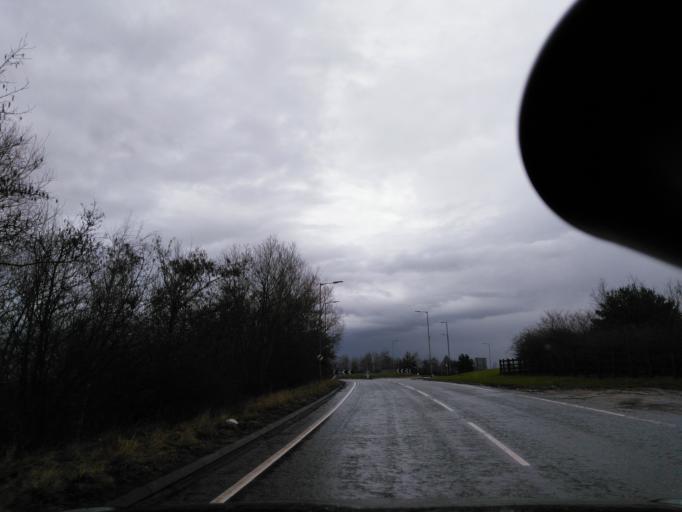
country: GB
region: England
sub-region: North Yorkshire
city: Boroughbridge
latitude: 54.1534
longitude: -1.4302
